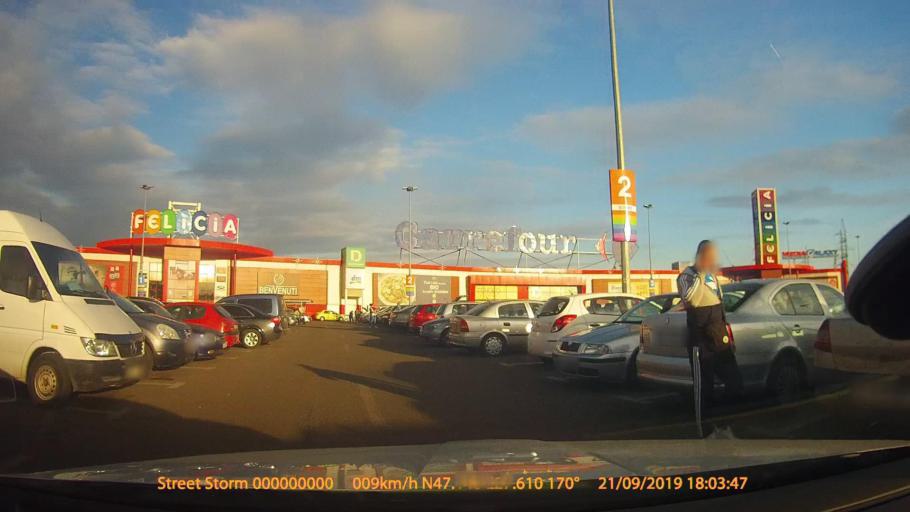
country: RO
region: Iasi
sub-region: Municipiul Iasi
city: Iasi
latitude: 47.1456
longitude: 27.6100
